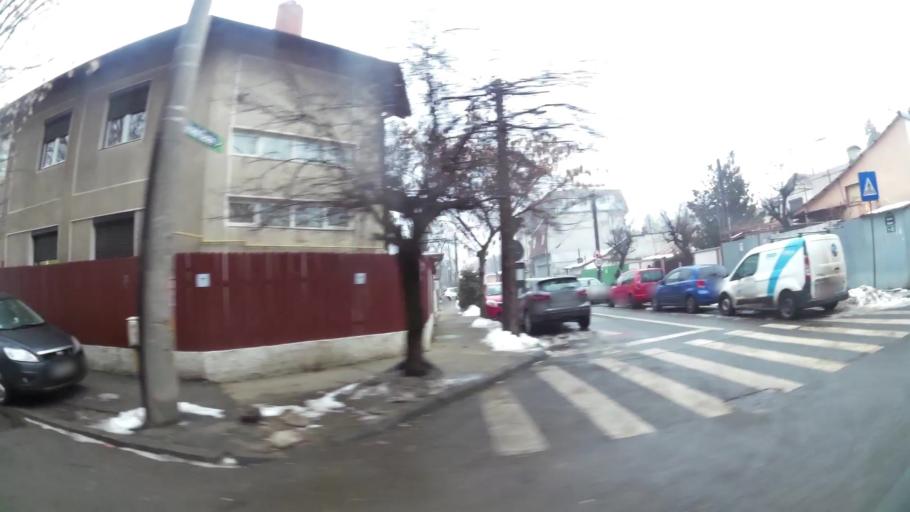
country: RO
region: Ilfov
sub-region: Comuna Chiajna
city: Rosu
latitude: 44.4742
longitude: 26.0524
